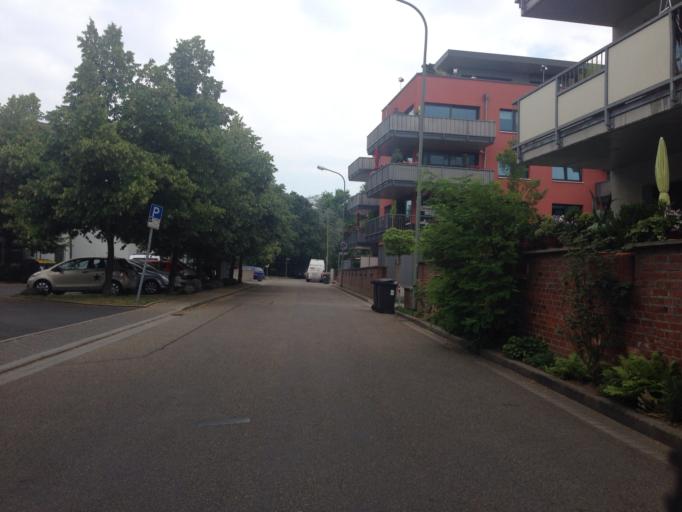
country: DE
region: Hesse
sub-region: Regierungsbezirk Darmstadt
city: Hanau am Main
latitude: 50.1481
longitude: 8.9050
